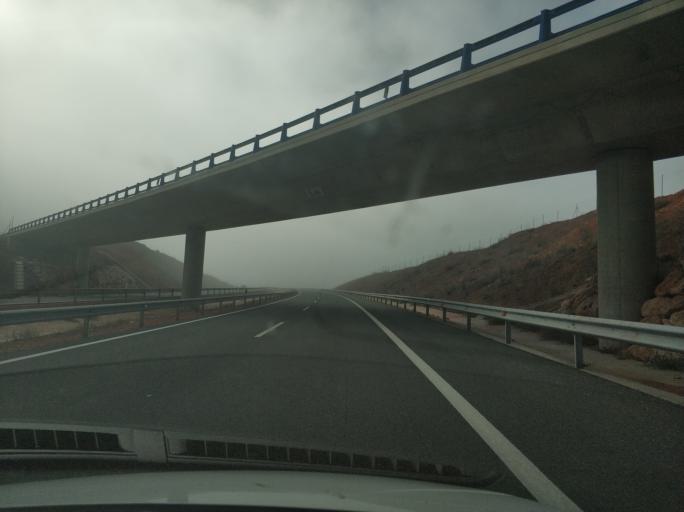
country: ES
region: Castille and Leon
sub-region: Provincia de Soria
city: Yelo
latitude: 41.2412
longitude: -2.4790
